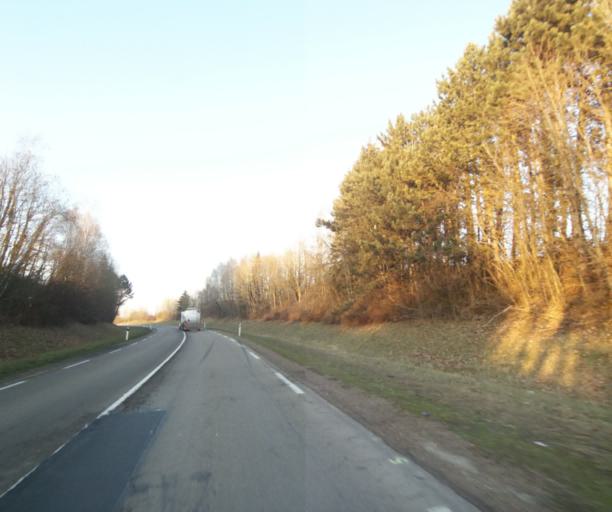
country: FR
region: Champagne-Ardenne
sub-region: Departement de la Haute-Marne
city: Bienville
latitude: 48.5756
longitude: 5.0355
